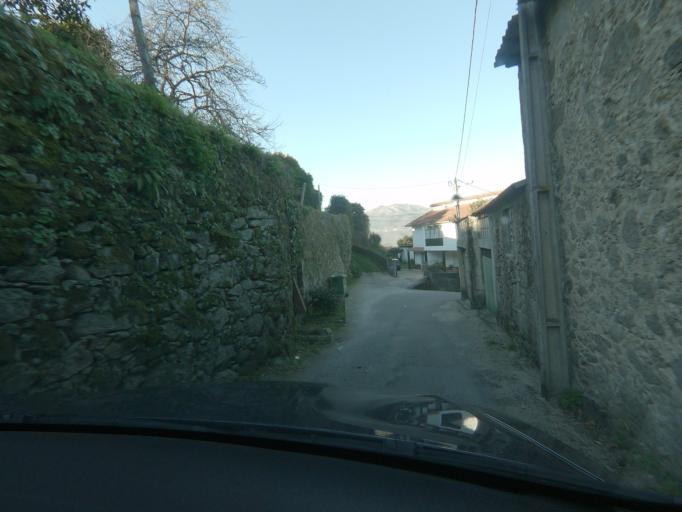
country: PT
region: Viseu
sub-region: Oliveira de Frades
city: Oliveira de Frades
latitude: 40.7315
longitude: -8.1575
